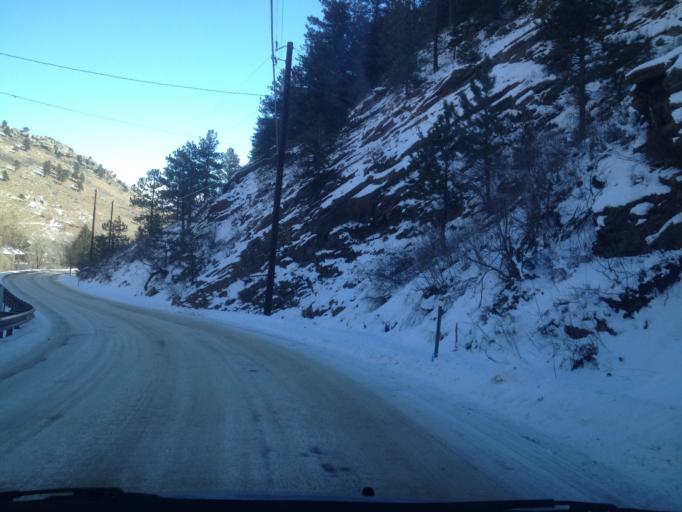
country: US
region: Colorado
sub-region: Boulder County
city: Boulder
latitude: 40.0642
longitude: -105.3062
